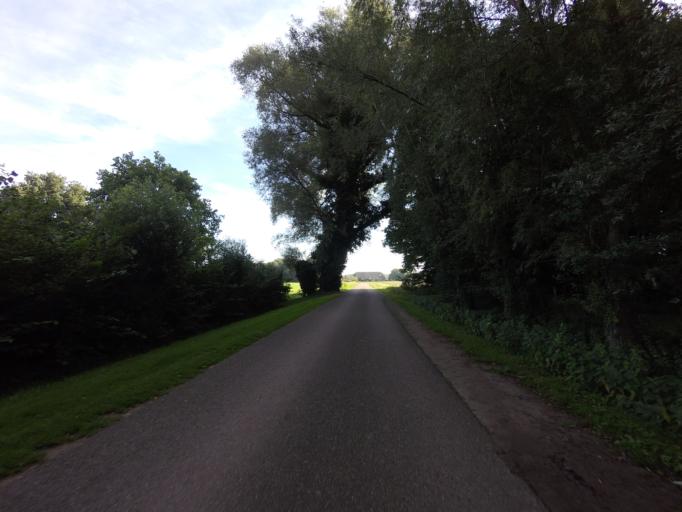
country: NL
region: Gelderland
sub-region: Oude IJsselstreek
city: Varsseveld
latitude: 51.9281
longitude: 6.4426
